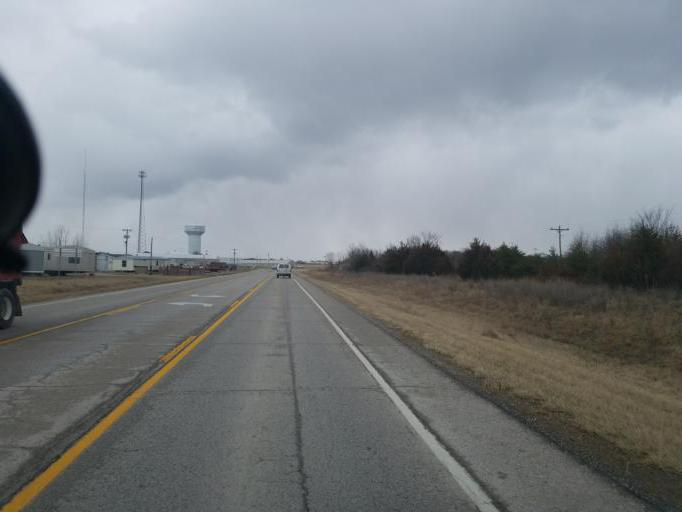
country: US
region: Missouri
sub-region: Macon County
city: Macon
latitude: 39.7658
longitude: -92.4691
